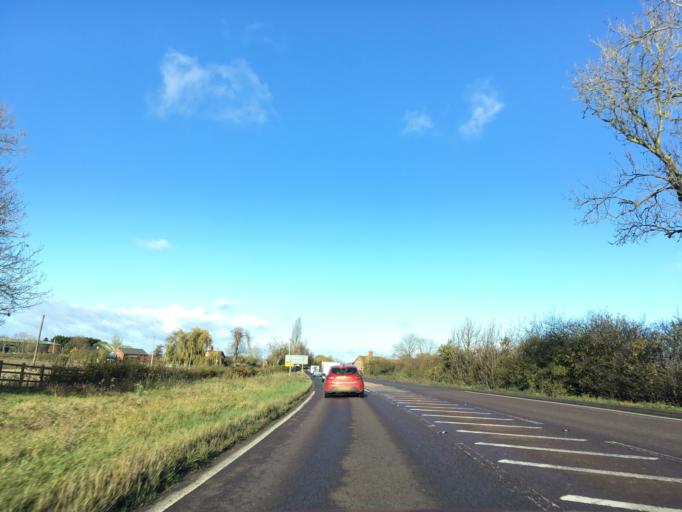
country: GB
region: England
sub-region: Worcestershire
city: Evesham
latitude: 52.0585
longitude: -1.9565
